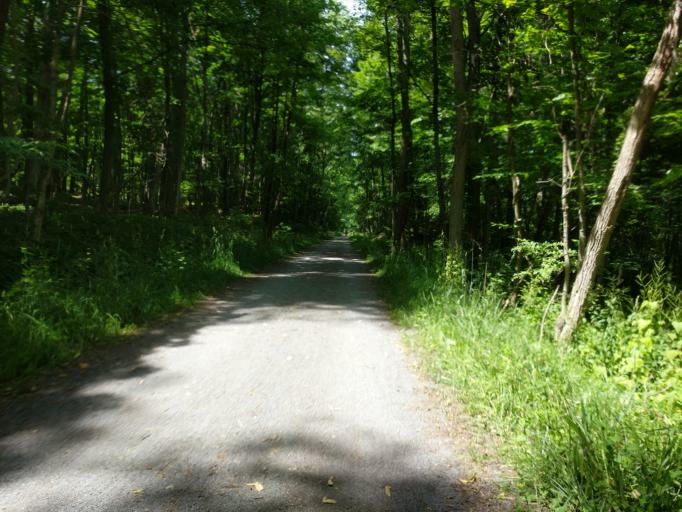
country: US
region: New York
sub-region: Tompkins County
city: Northwest Ithaca
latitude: 42.4844
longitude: -76.5380
